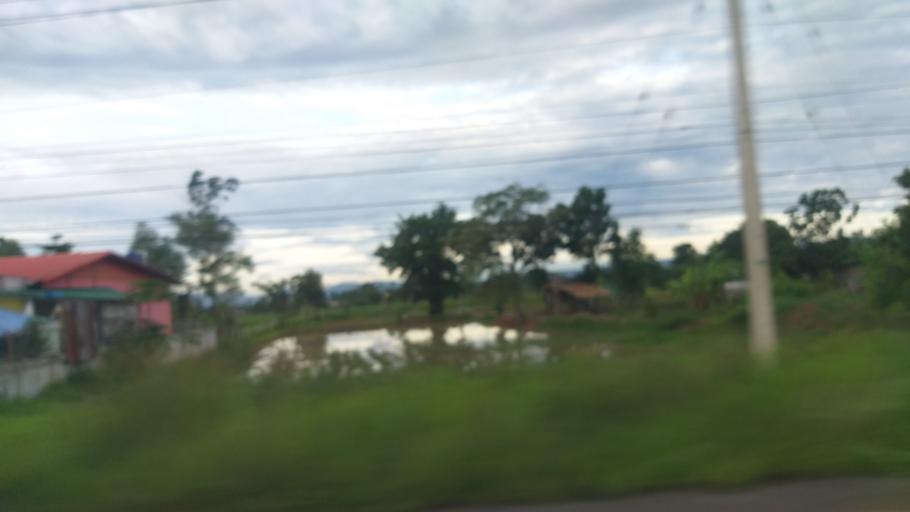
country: TH
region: Chaiyaphum
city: Kaeng Khro
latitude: 16.1691
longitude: 102.2202
